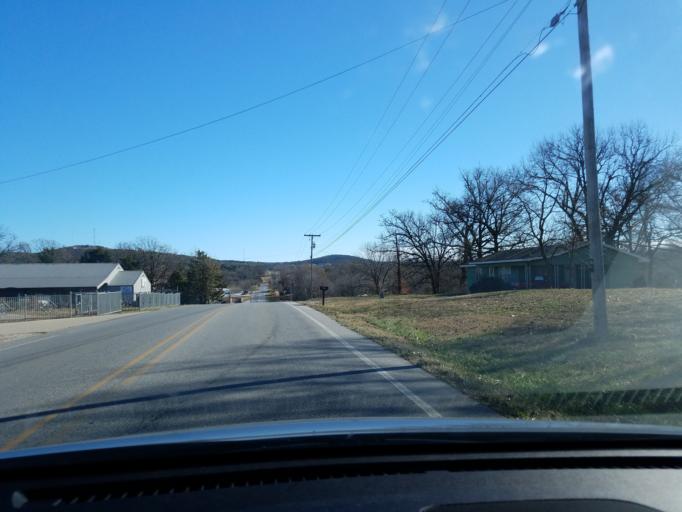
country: US
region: Arkansas
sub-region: Carroll County
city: Berryville
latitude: 36.3781
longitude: -93.5804
